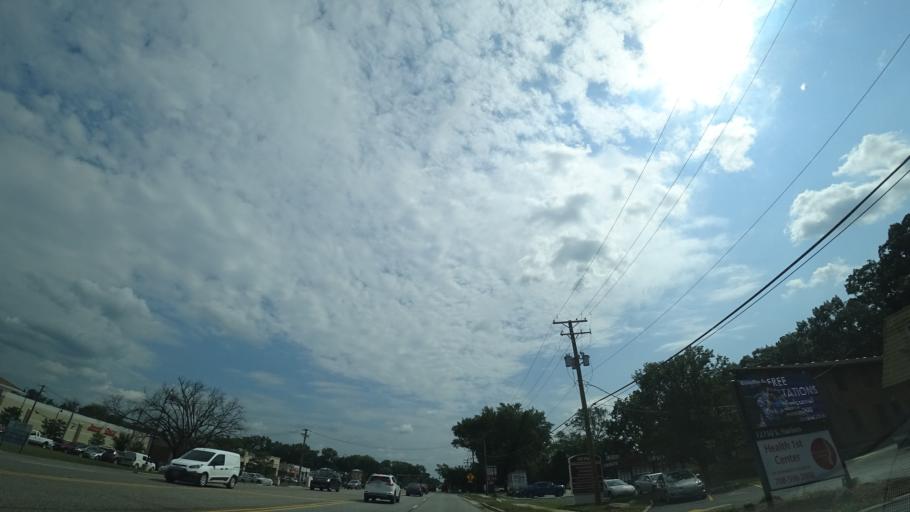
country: US
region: Illinois
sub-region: Cook County
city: Palos Heights
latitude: 41.6599
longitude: -87.7964
